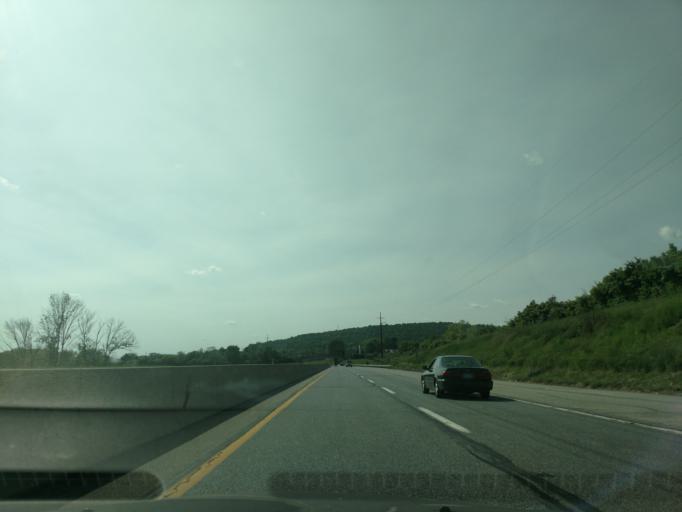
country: US
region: Pennsylvania
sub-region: Lancaster County
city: Swartzville
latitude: 40.2219
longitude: -76.0913
